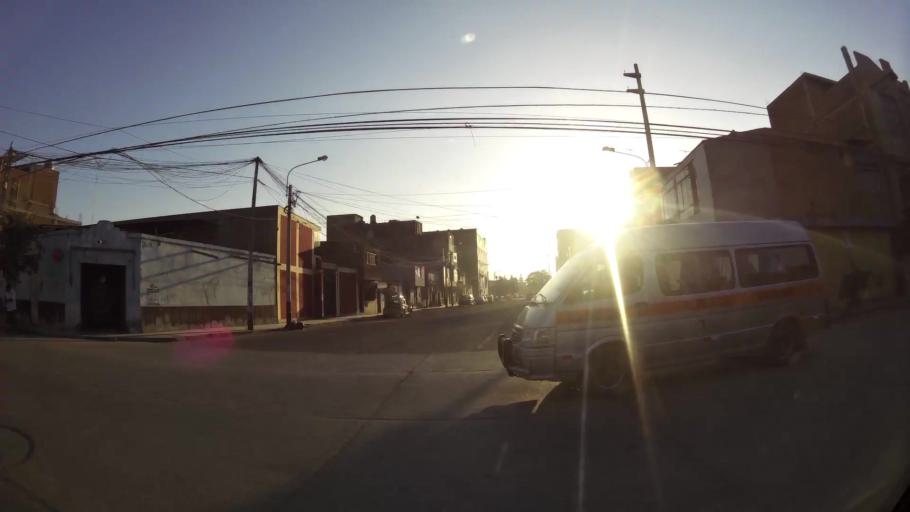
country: PE
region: Lambayeque
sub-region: Provincia de Chiclayo
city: Santa Rosa
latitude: -6.7721
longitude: -79.8295
